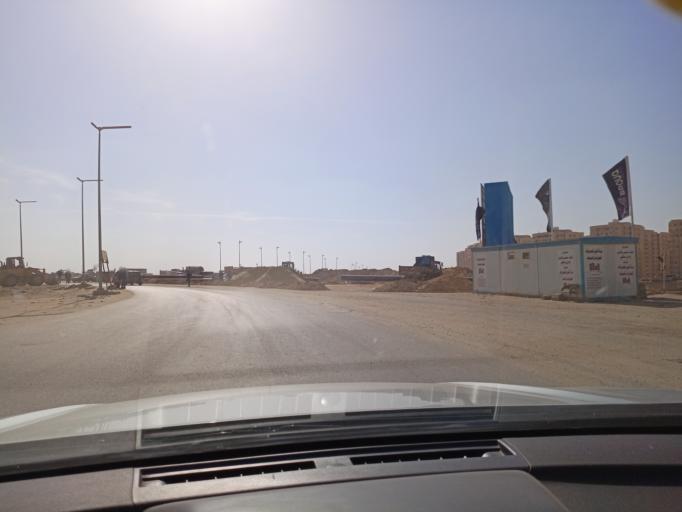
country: EG
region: Muhafazat al Qalyubiyah
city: Al Khankah
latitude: 30.0246
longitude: 31.6772
